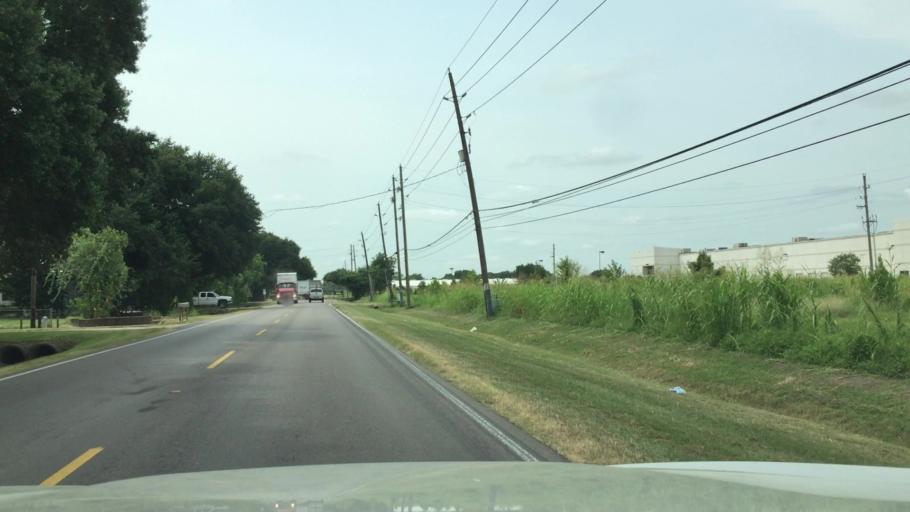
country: US
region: Texas
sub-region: Harris County
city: Jersey Village
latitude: 29.9240
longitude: -95.5480
